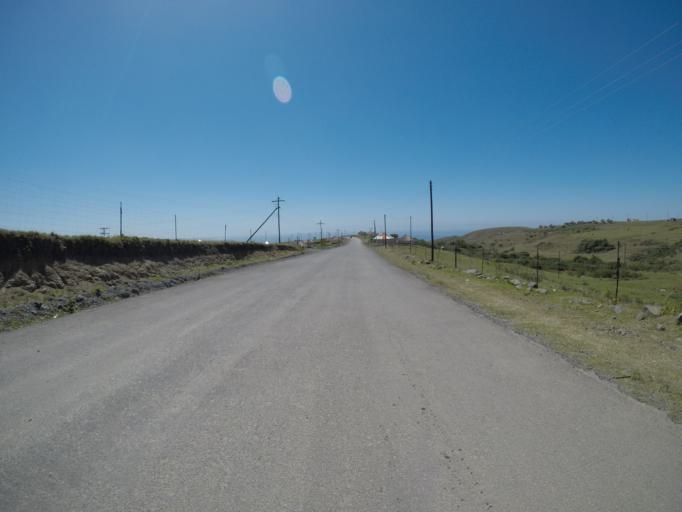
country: ZA
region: Eastern Cape
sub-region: OR Tambo District Municipality
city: Libode
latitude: -31.9971
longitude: 29.1236
